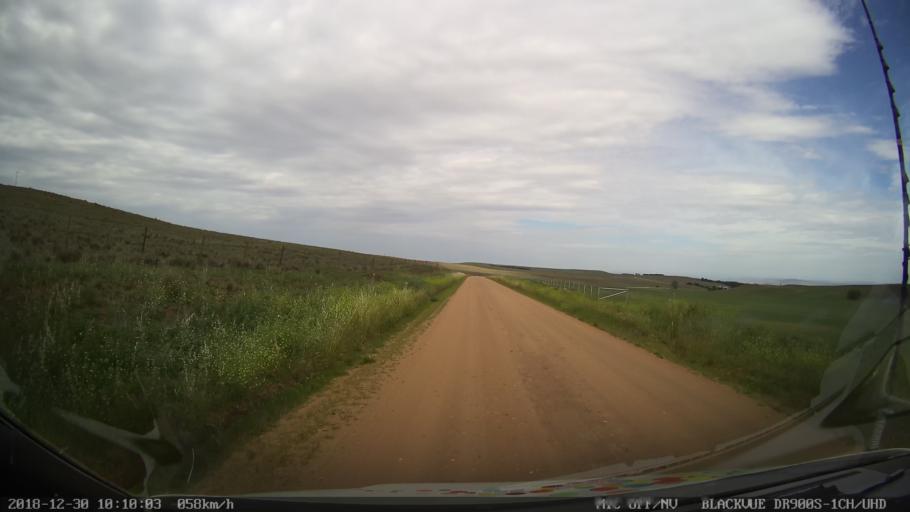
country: AU
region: New South Wales
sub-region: Cooma-Monaro
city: Cooma
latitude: -36.5502
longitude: 149.0988
